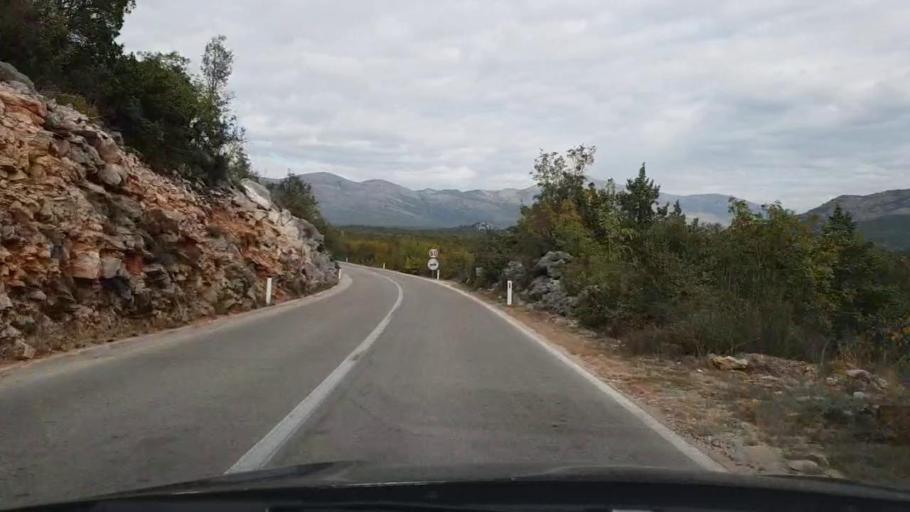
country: HR
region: Dubrovacko-Neretvanska
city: Cibaca
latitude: 42.6713
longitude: 18.2304
